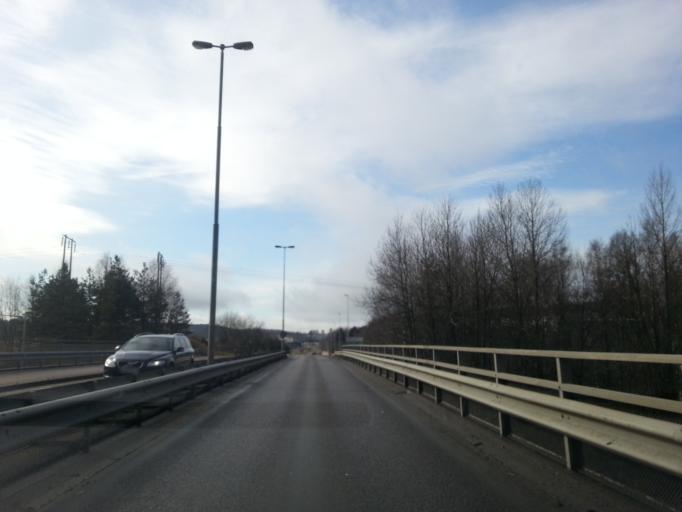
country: SE
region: Vaestra Goetaland
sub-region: Kungalvs Kommun
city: Kungalv
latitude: 57.8846
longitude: 11.9457
